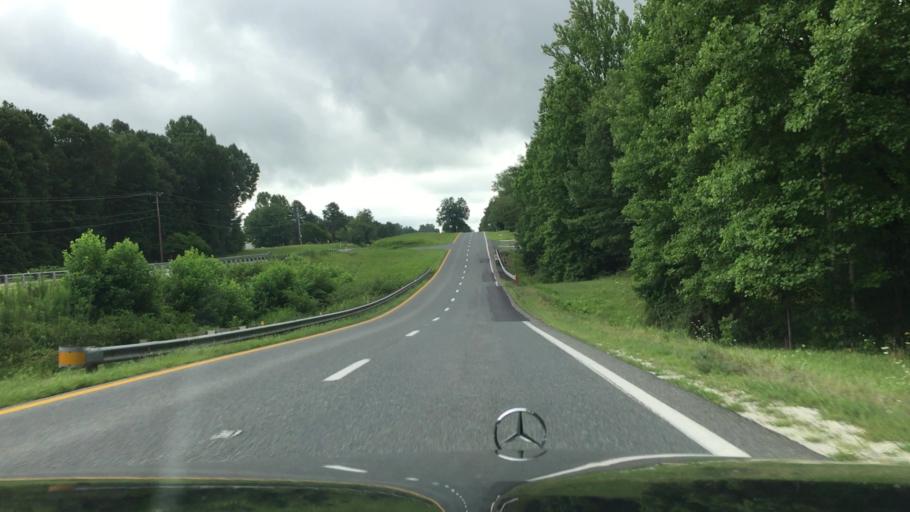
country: US
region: Virginia
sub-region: Appomattox County
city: Appomattox
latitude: 37.2991
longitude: -78.7424
